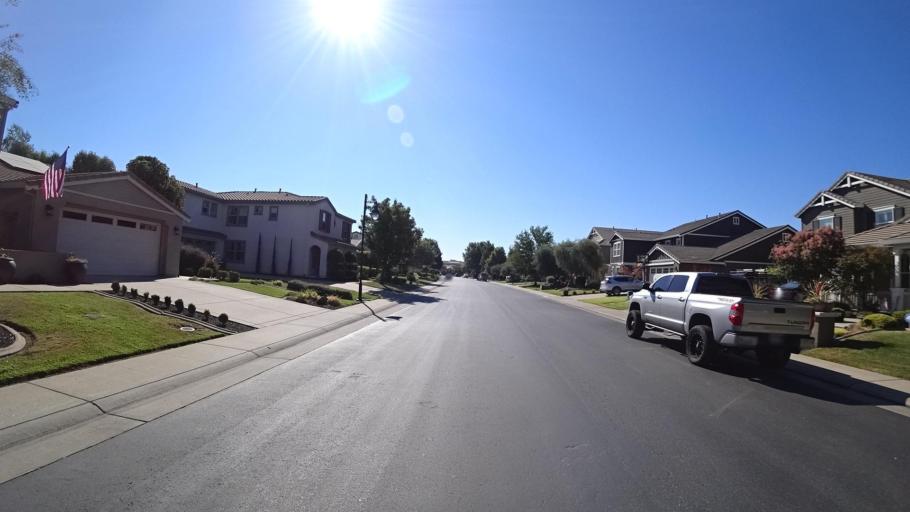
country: US
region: California
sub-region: Placer County
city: Lincoln
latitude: 38.8354
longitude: -121.2782
